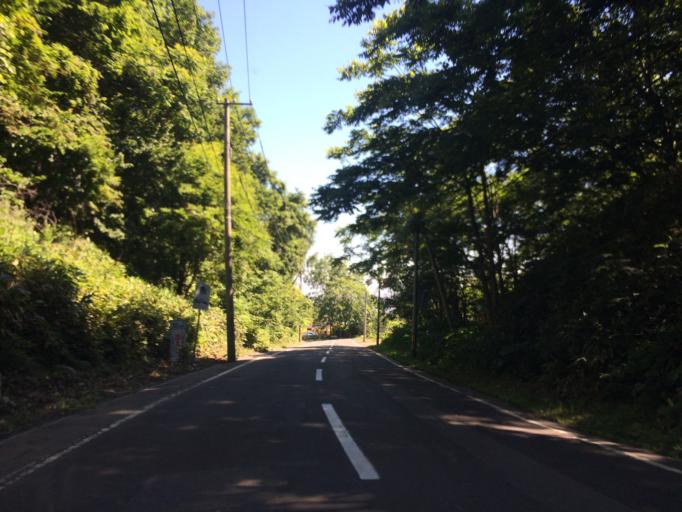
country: JP
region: Hokkaido
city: Sapporo
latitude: 43.0367
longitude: 141.2855
